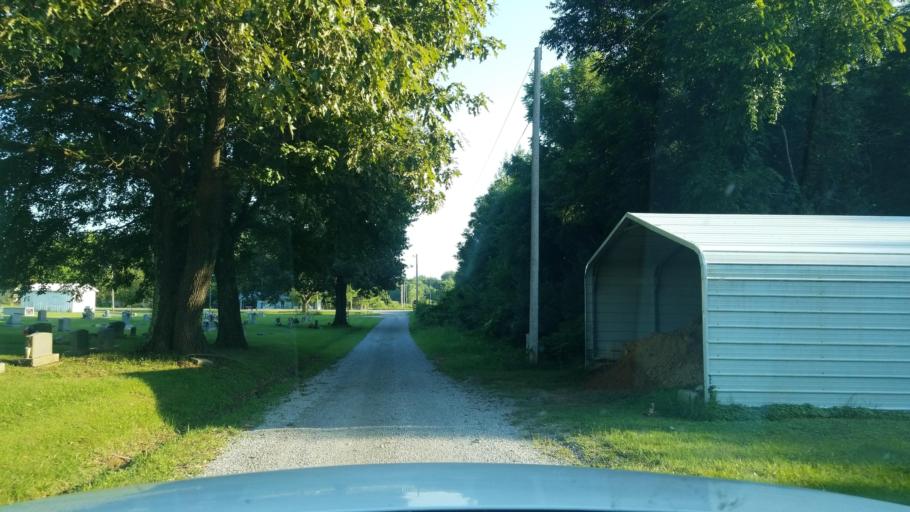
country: US
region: Illinois
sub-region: Saline County
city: Eldorado
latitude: 37.8200
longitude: -88.4597
